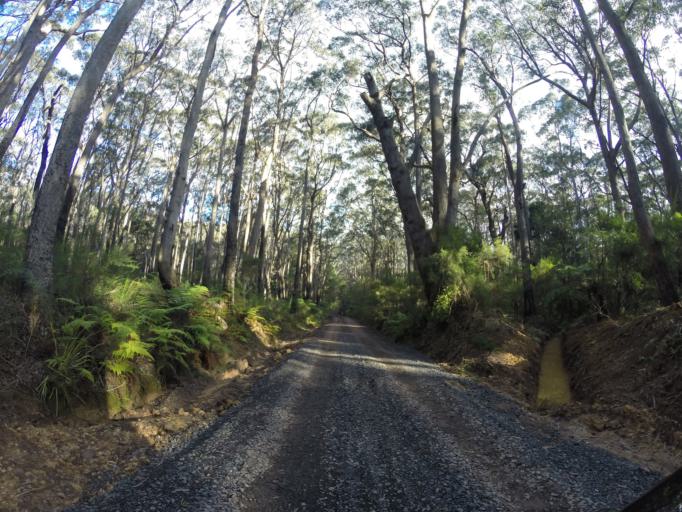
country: AU
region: New South Wales
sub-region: Wollongong
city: Cordeaux Heights
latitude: -34.4111
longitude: 150.7850
